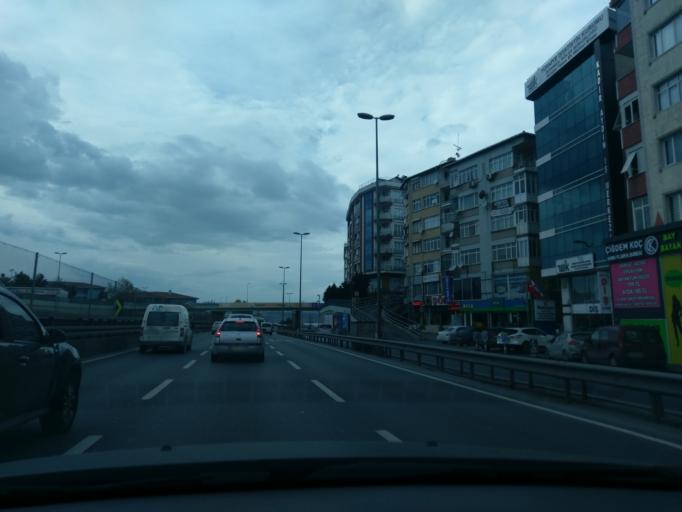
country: TR
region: Istanbul
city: Bahcelievler
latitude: 40.9854
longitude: 28.7815
